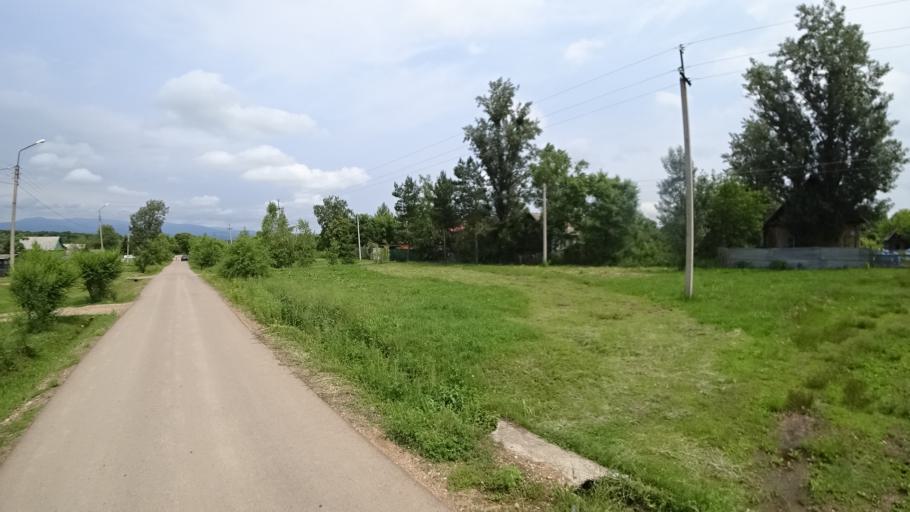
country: RU
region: Primorskiy
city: Novosysoyevka
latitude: 44.2368
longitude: 133.3586
